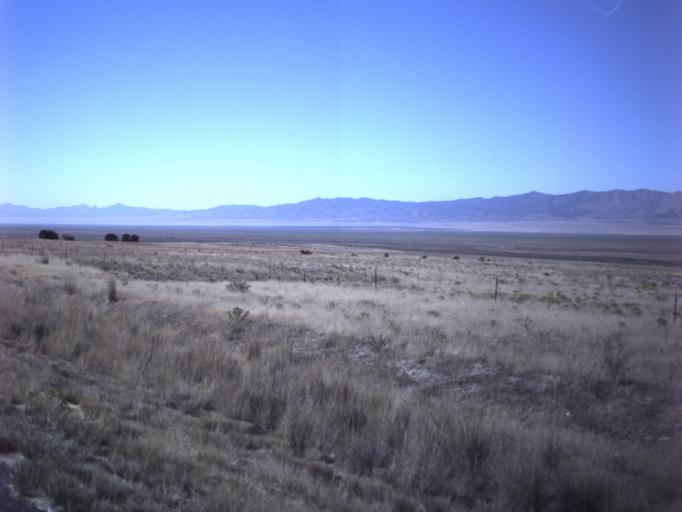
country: US
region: Utah
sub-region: Tooele County
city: Grantsville
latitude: 40.5877
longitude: -112.7221
